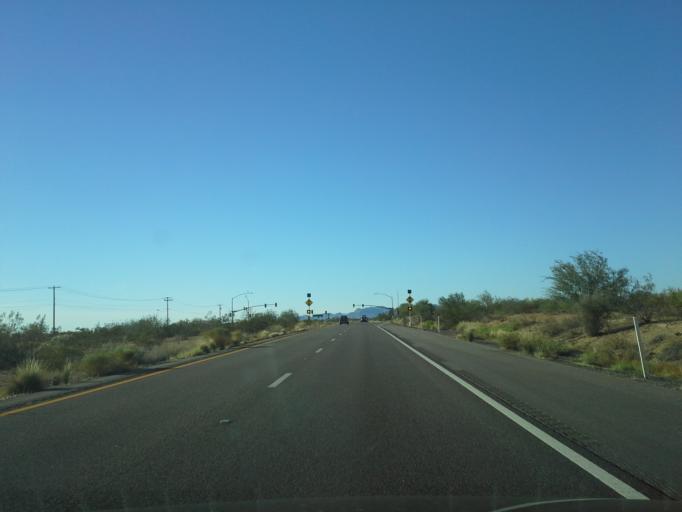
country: US
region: Arizona
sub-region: Pinal County
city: Apache Junction
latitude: 33.3344
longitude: -111.4385
